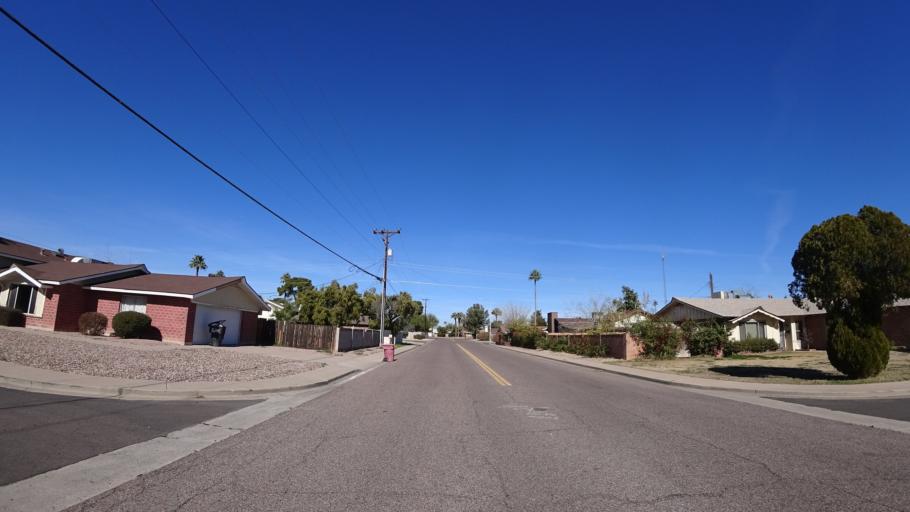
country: US
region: Arizona
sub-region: Maricopa County
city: Scottsdale
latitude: 33.5188
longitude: -111.8960
